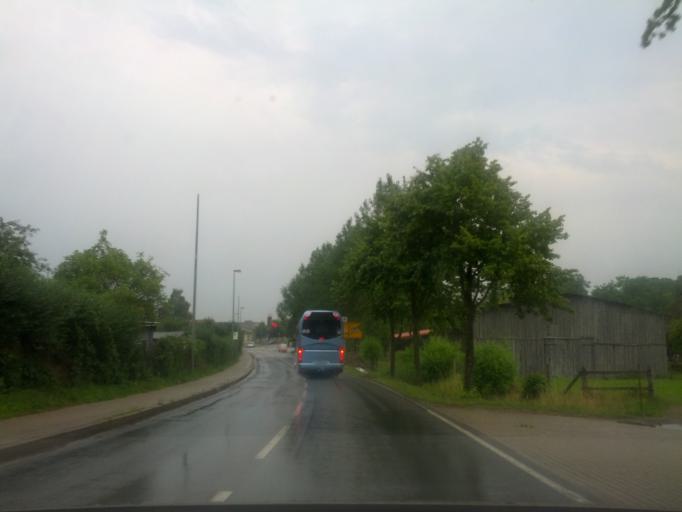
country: DE
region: Mecklenburg-Vorpommern
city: Ostseebad Kuhlungsborn
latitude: 54.1386
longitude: 11.7477
